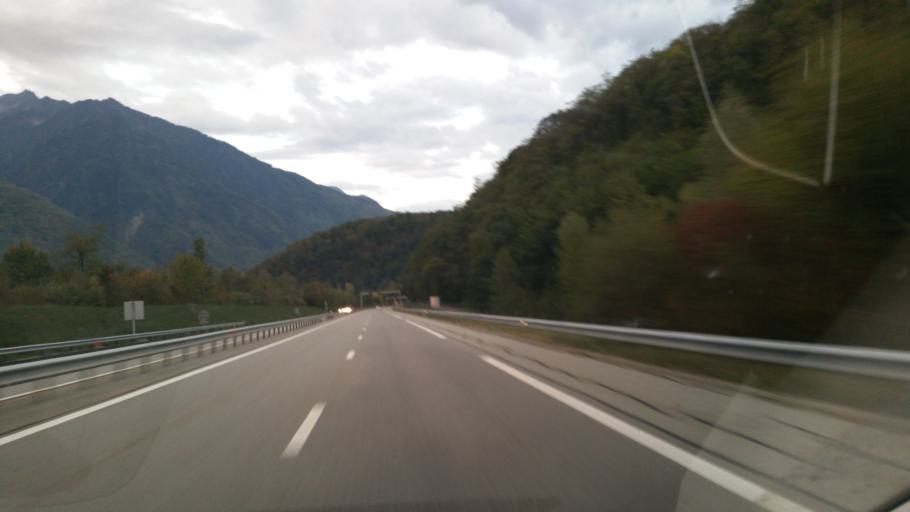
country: FR
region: Rhone-Alpes
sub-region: Departement de la Savoie
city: Aiton
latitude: 45.5263
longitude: 6.3085
